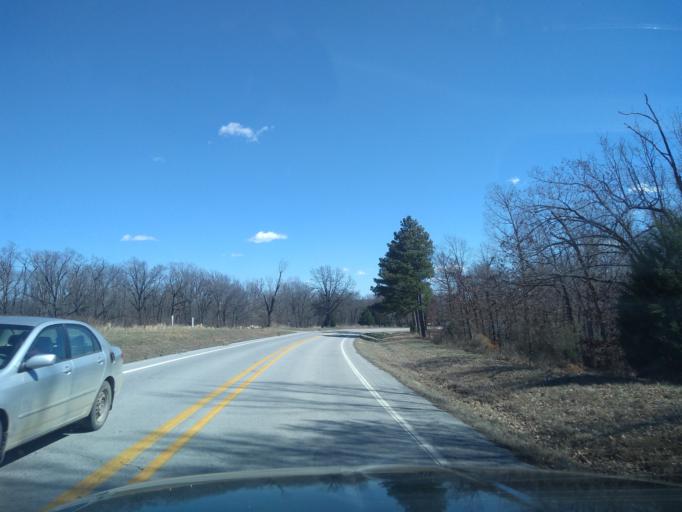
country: US
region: Arkansas
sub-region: Washington County
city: Farmington
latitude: 36.0818
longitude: -94.3130
